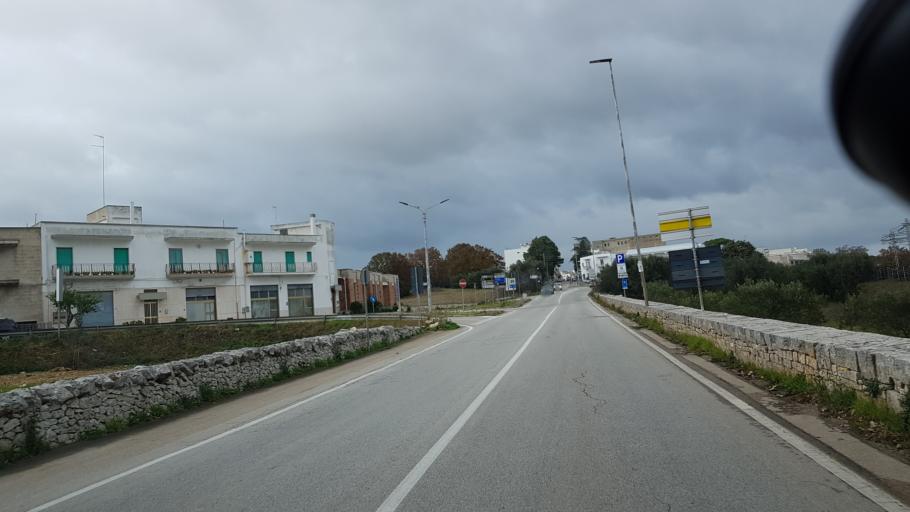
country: IT
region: Apulia
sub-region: Provincia di Bari
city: Alberobello
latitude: 40.7817
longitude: 17.2447
